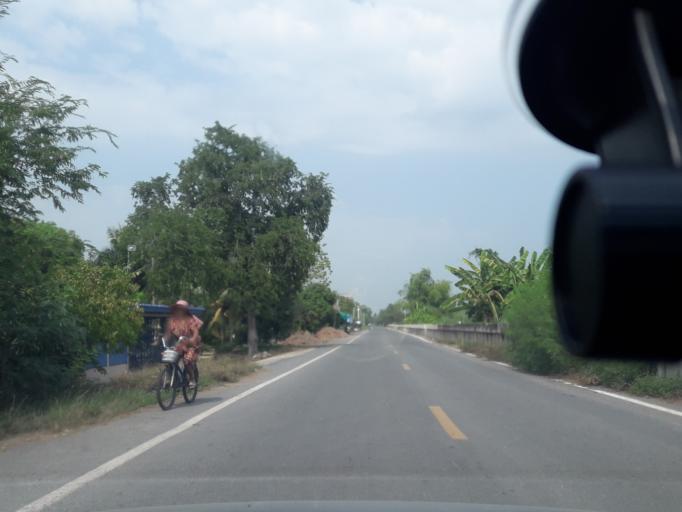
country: TH
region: Sara Buri
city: Nong Khae
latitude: 14.2504
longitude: 100.8913
